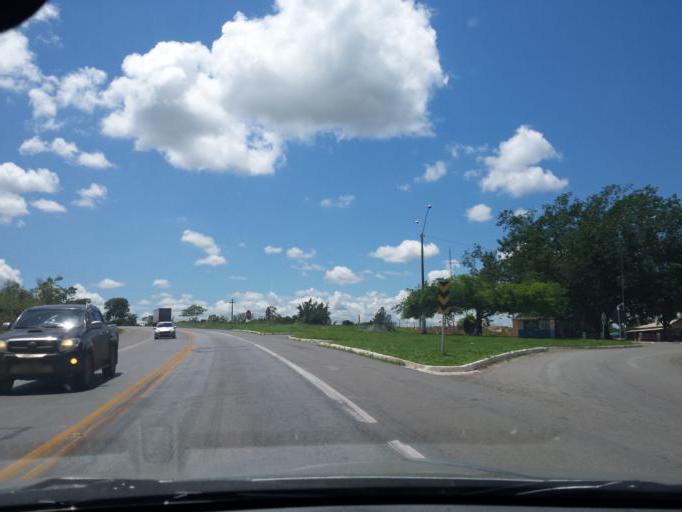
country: BR
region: Goias
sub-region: Cristalina
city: Cristalina
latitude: -16.5391
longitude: -47.7978
